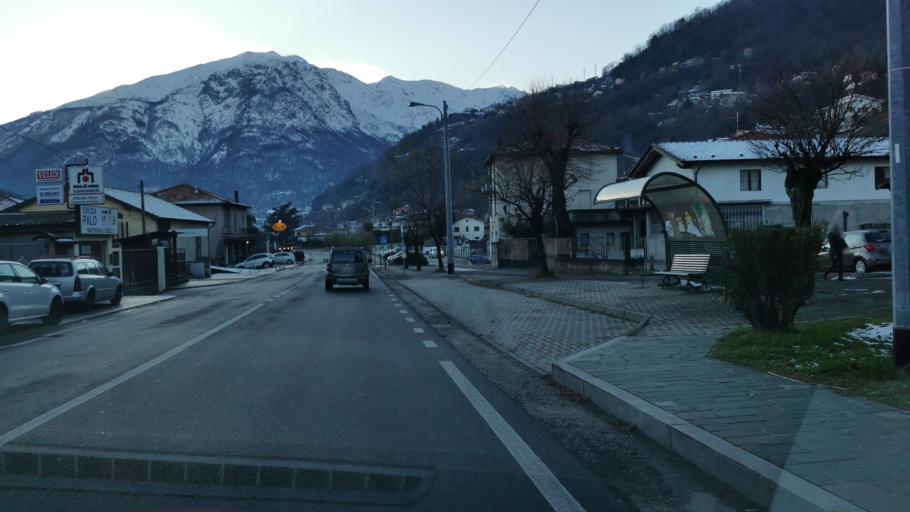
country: IT
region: Lombardy
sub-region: Provincia di Como
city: Consiglio di Rumo
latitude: 46.1415
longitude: 9.2937
